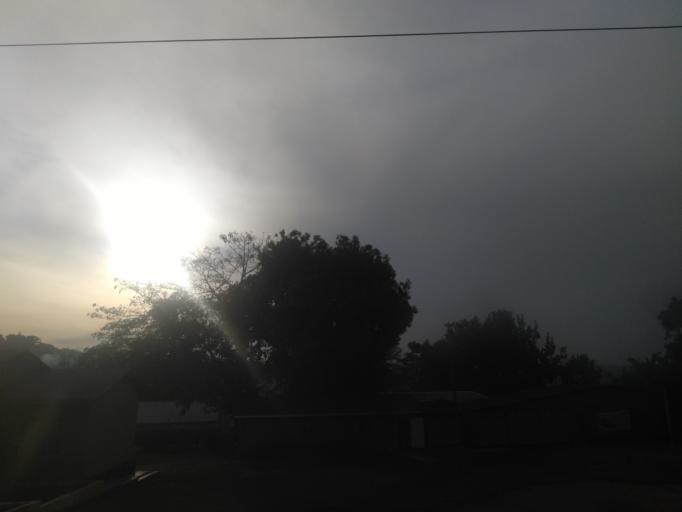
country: UG
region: Central Region
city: Kampala Central Division
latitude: 0.3453
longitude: 32.5735
